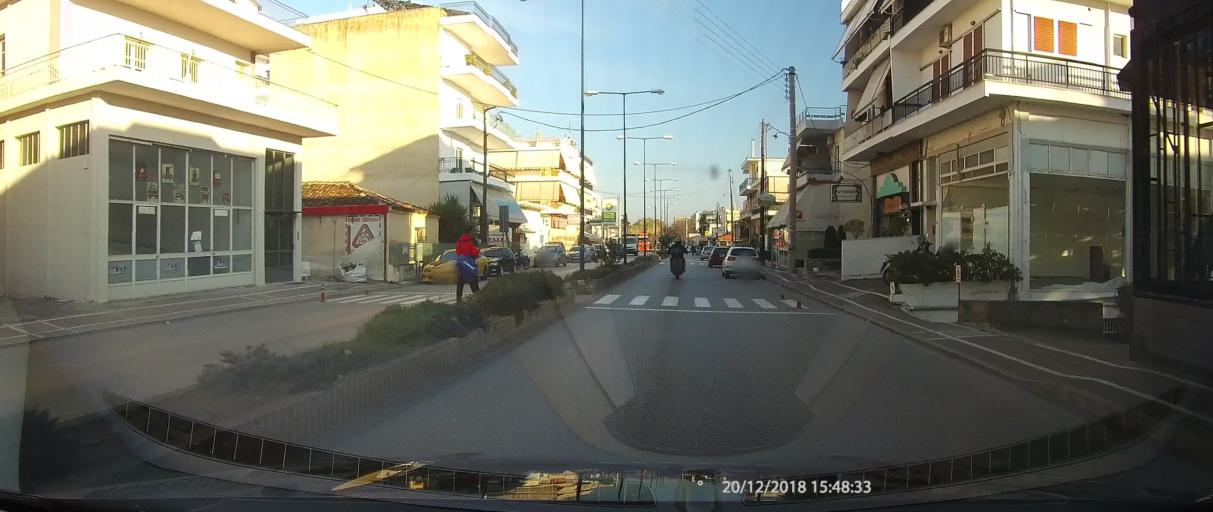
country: GR
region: Central Greece
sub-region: Nomos Fthiotidos
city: Lamia
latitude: 38.8943
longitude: 22.4409
